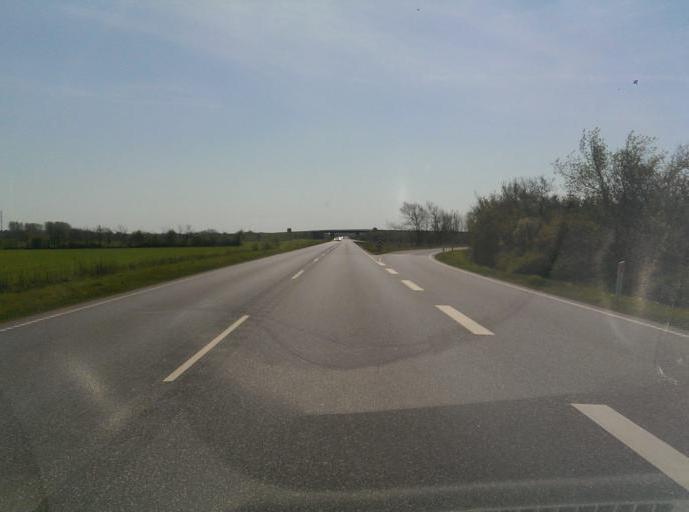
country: DK
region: South Denmark
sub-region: Esbjerg Kommune
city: Bramming
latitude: 55.4087
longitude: 8.7213
